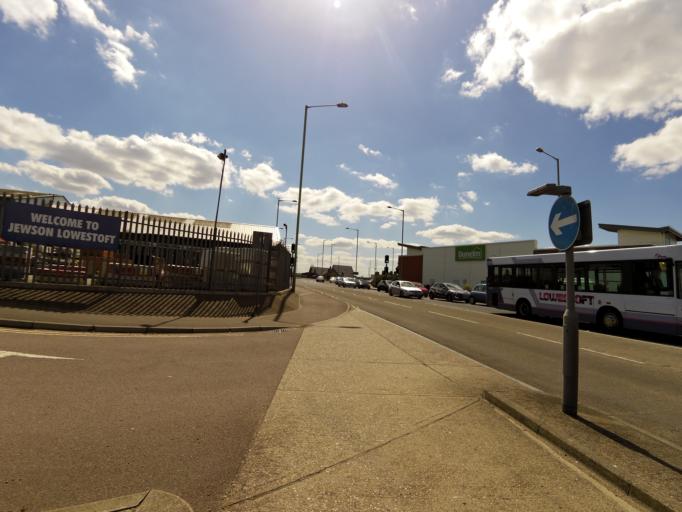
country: GB
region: England
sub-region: Suffolk
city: Lowestoft
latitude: 52.4716
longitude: 1.7447
